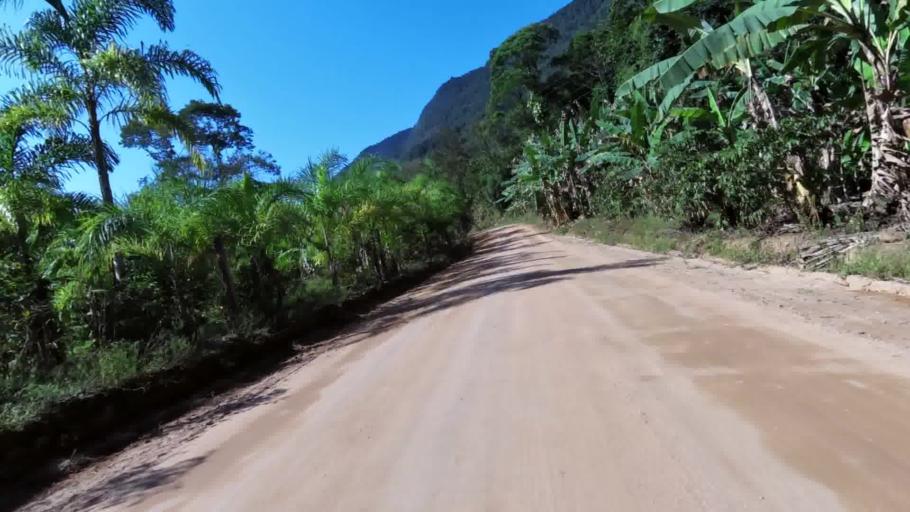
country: BR
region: Espirito Santo
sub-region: Alfredo Chaves
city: Alfredo Chaves
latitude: -20.5621
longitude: -40.7323
